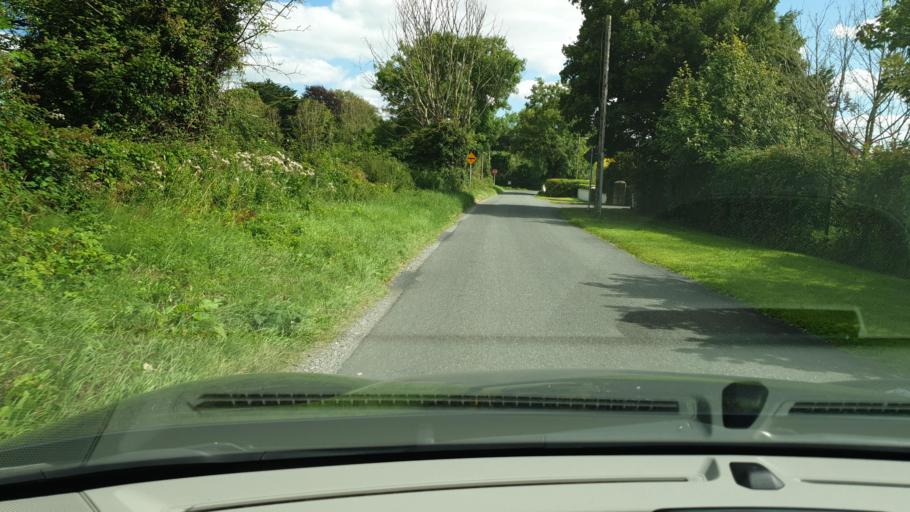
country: IE
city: Confey
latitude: 53.3977
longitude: -6.4992
